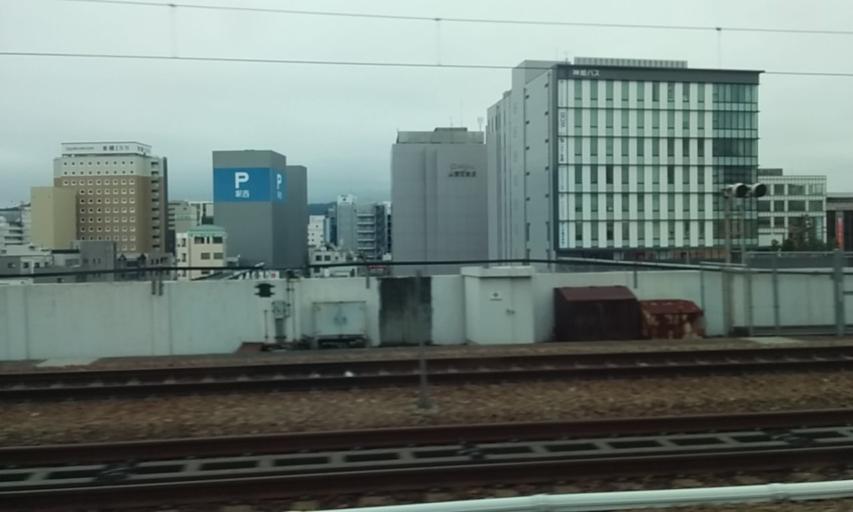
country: JP
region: Hyogo
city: Himeji
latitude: 34.8266
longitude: 134.6883
